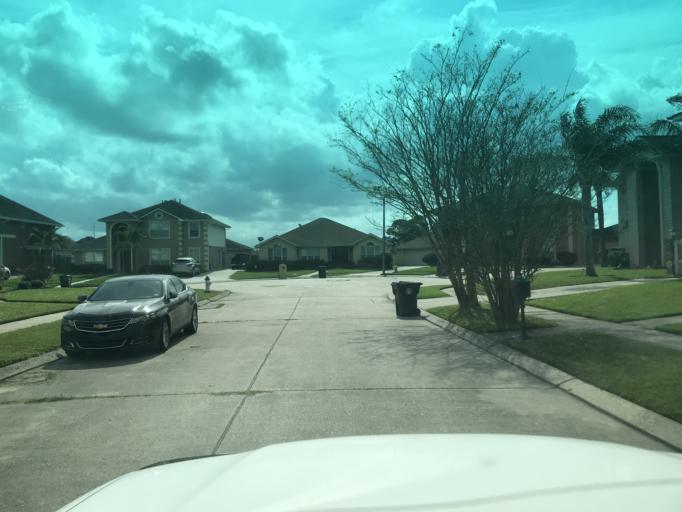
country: US
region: Louisiana
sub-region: Saint Bernard Parish
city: Chalmette
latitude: 30.0318
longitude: -89.9531
